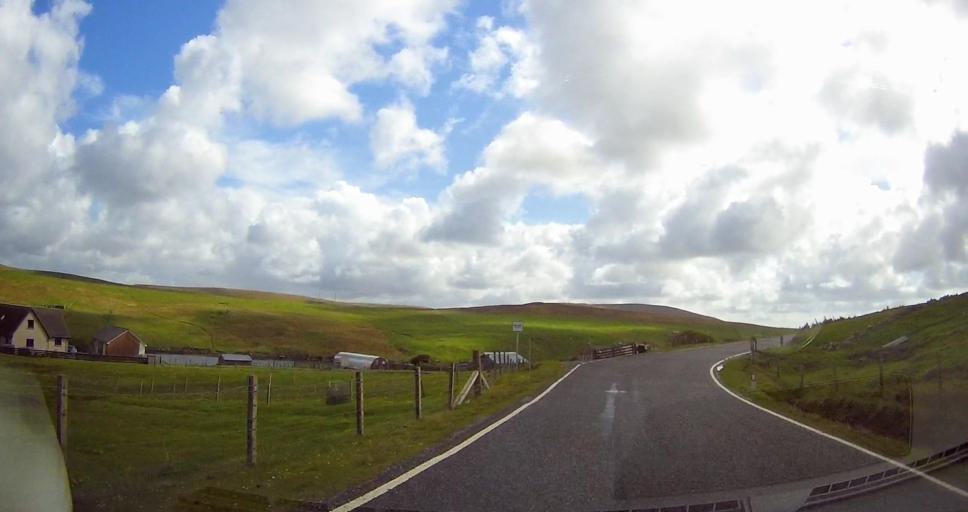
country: GB
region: Scotland
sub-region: Shetland Islands
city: Lerwick
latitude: 60.5311
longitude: -1.3625
